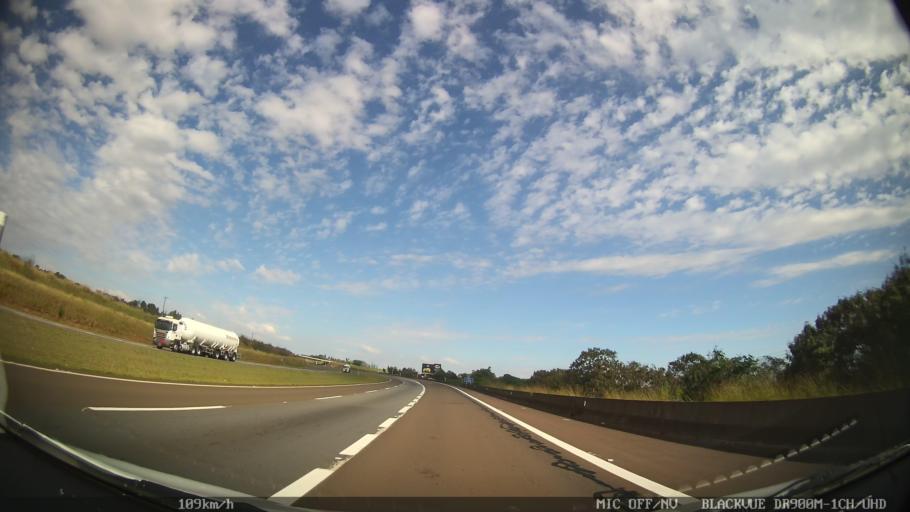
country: BR
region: Sao Paulo
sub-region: Iracemapolis
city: Iracemapolis
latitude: -22.5800
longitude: -47.4598
